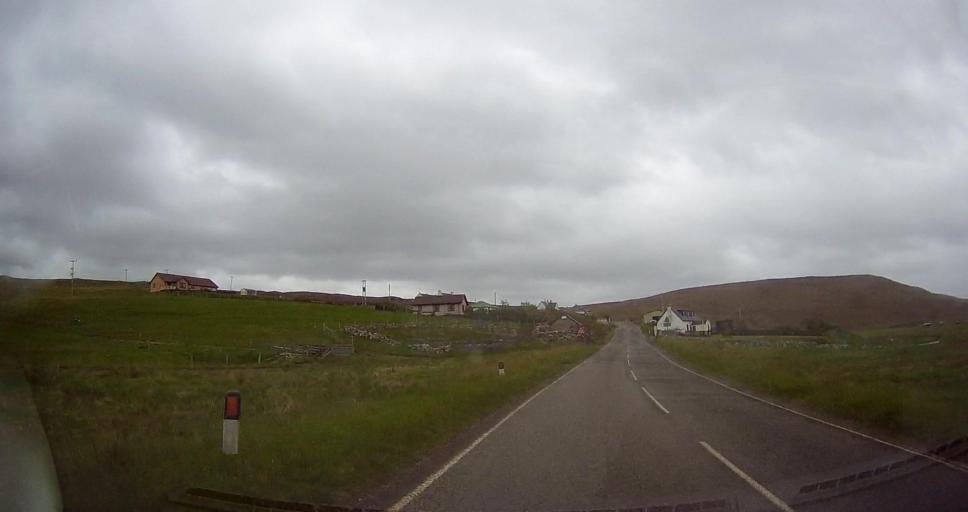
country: GB
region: Scotland
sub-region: Shetland Islands
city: Lerwick
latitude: 60.4915
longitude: -1.4533
